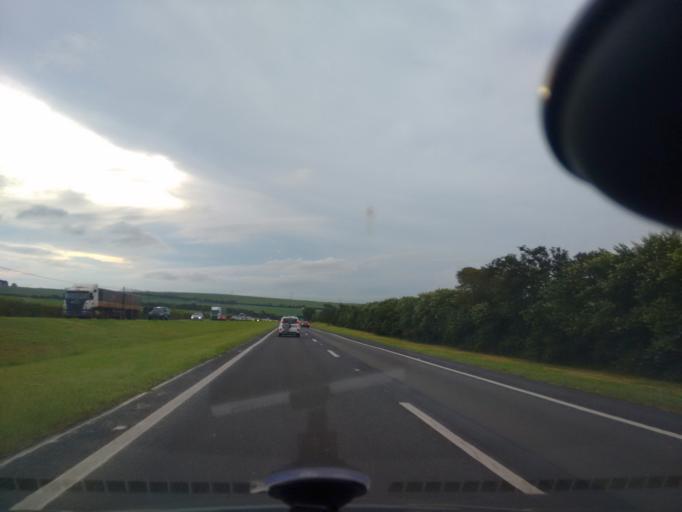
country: BR
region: Sao Paulo
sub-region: Itirapina
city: Itirapina
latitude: -22.2254
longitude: -47.7524
